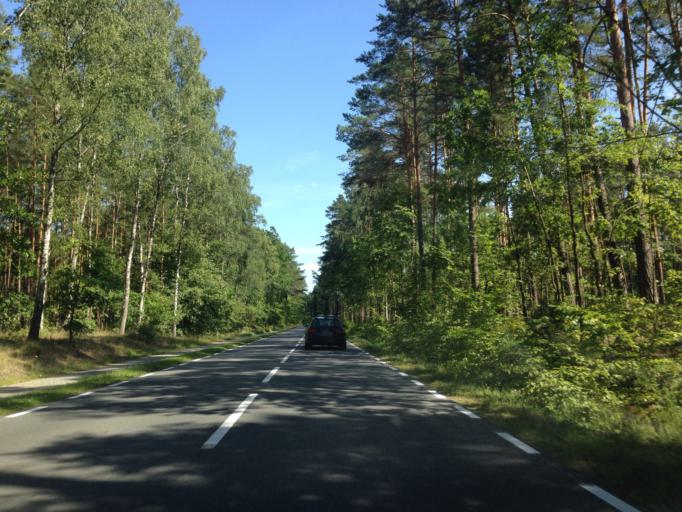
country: PL
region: Kujawsko-Pomorskie
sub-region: Powiat swiecki
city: Osie
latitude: 53.6074
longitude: 18.3140
